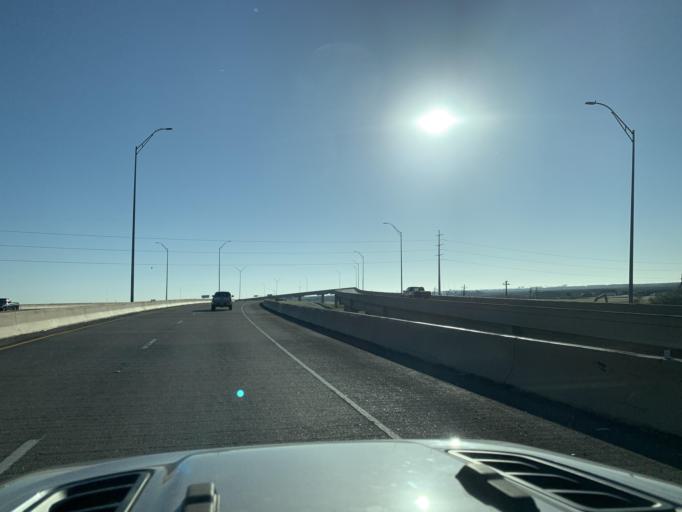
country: US
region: Texas
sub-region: Nueces County
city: Corpus Christi
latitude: 27.7847
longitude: -97.4873
